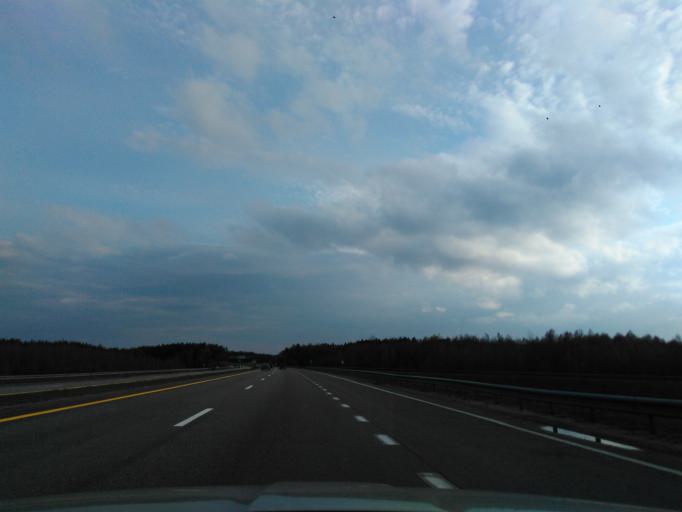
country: BY
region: Minsk
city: Astrashytski Haradok
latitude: 54.0537
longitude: 27.7038
